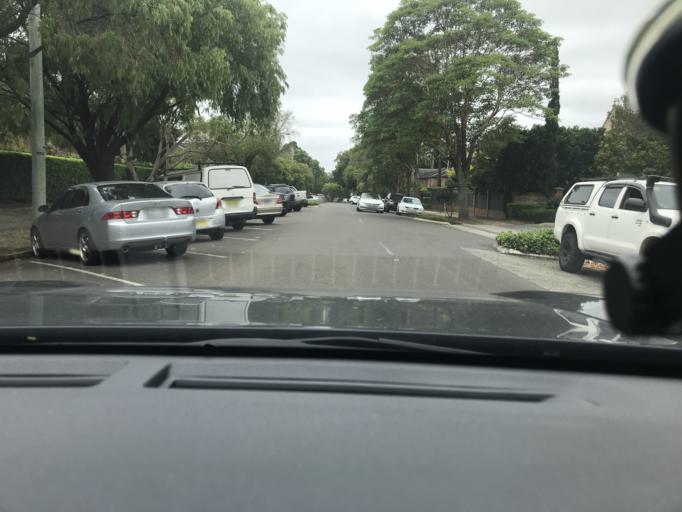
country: AU
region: New South Wales
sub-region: Canada Bay
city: Wareemba
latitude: -33.8582
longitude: 151.1189
